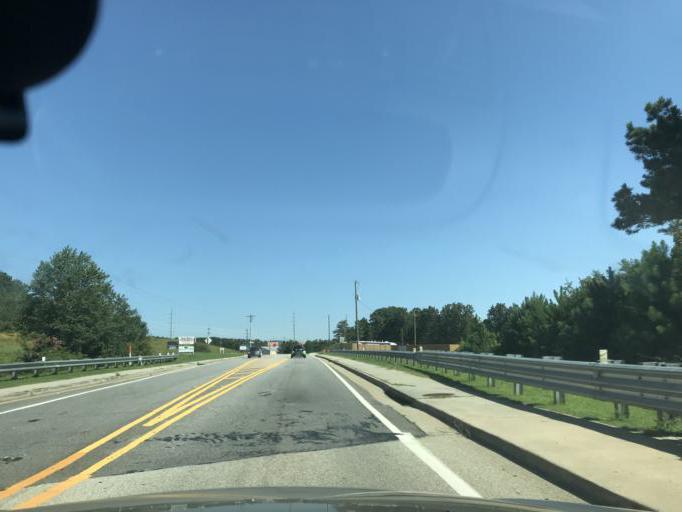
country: US
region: Georgia
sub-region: Forsyth County
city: Cumming
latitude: 34.1942
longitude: -84.1320
